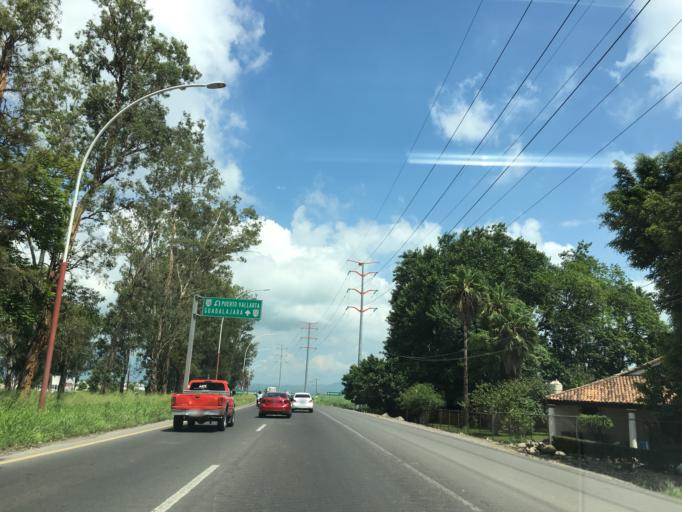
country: MX
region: Nayarit
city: Xalisco
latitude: 21.4687
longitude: -104.8859
